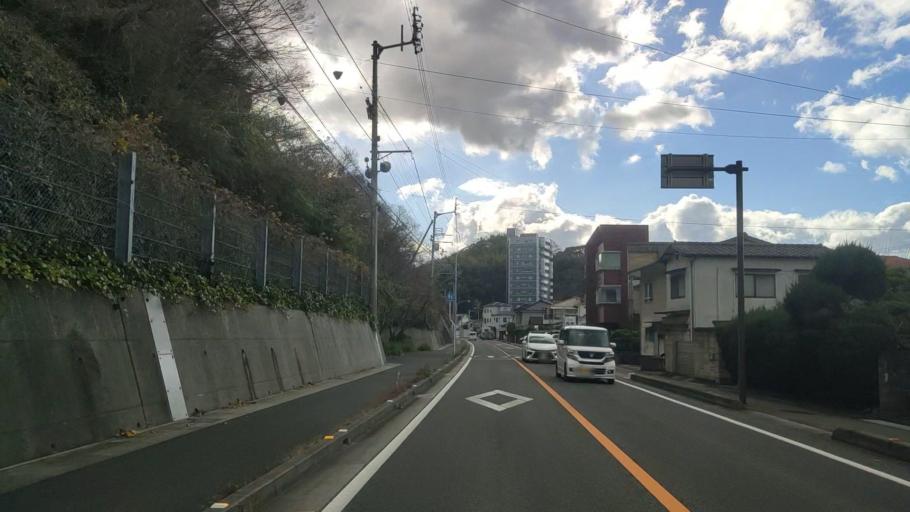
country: JP
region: Ehime
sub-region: Shikoku-chuo Shi
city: Matsuyama
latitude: 33.8721
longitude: 132.7097
